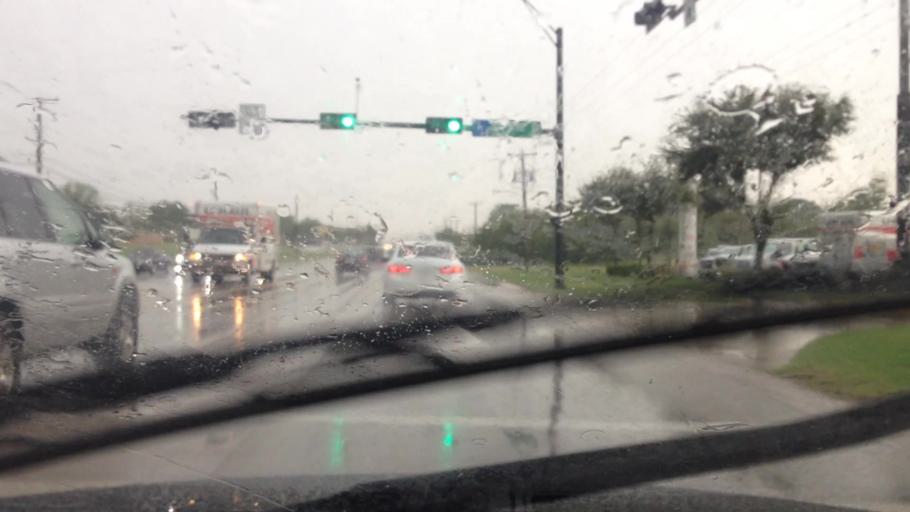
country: US
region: Texas
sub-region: Tarrant County
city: North Richland Hills
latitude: 32.8412
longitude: -97.2043
